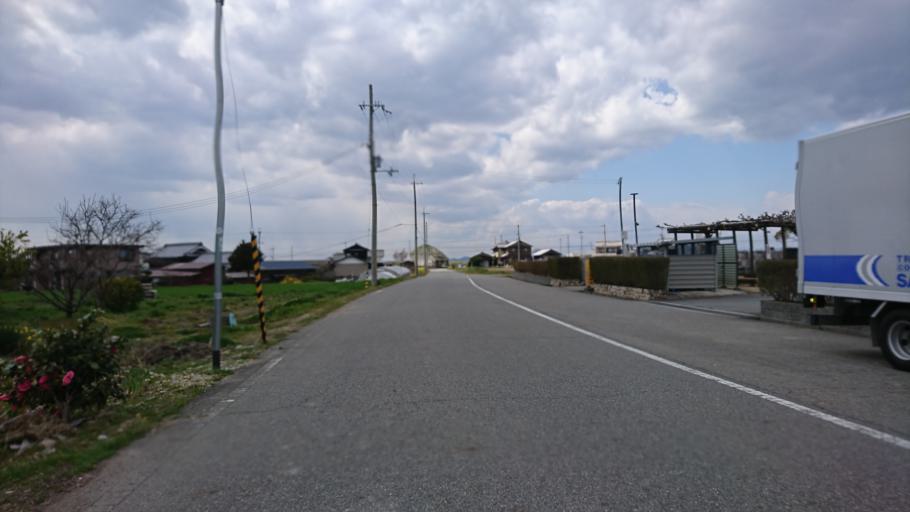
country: JP
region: Hyogo
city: Kakogawacho-honmachi
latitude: 34.7575
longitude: 134.9016
